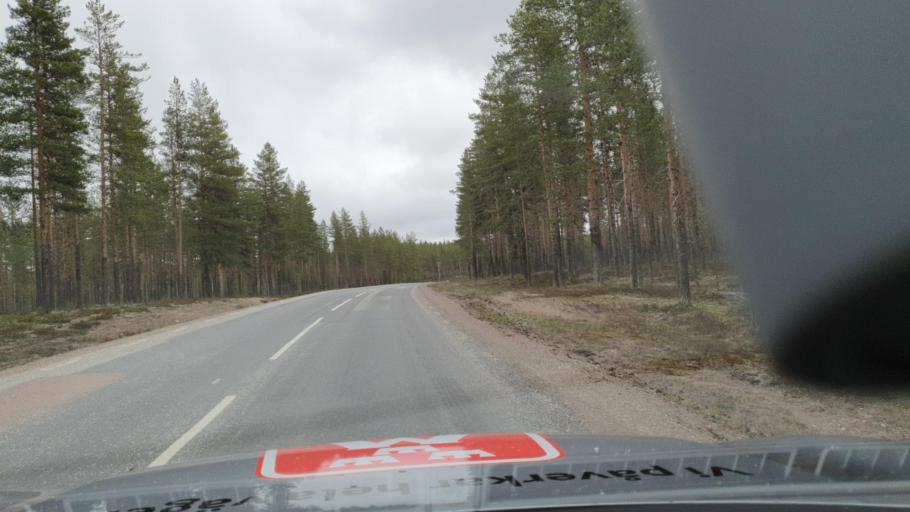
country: SE
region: Vaesternorrland
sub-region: Solleftea Kommun
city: Solleftea
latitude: 63.6408
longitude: 17.4089
